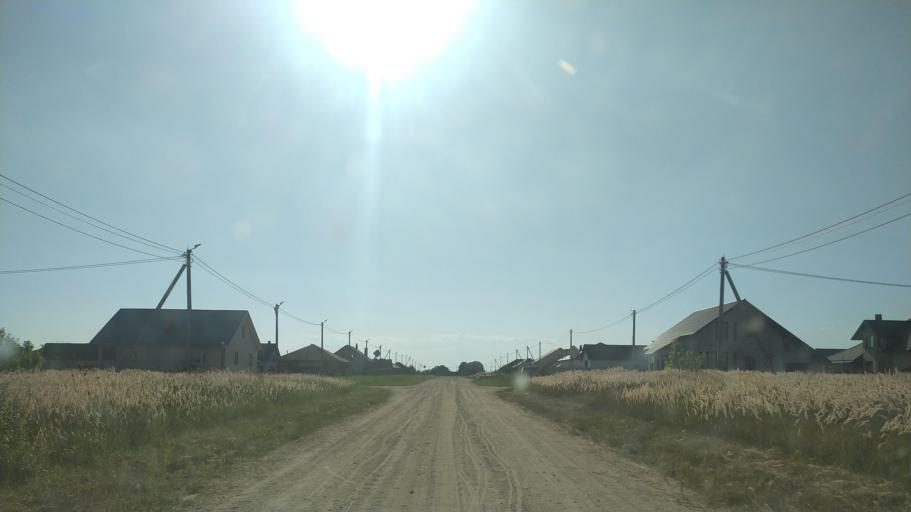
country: BY
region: Brest
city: Byaroza
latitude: 52.5148
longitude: 24.9749
